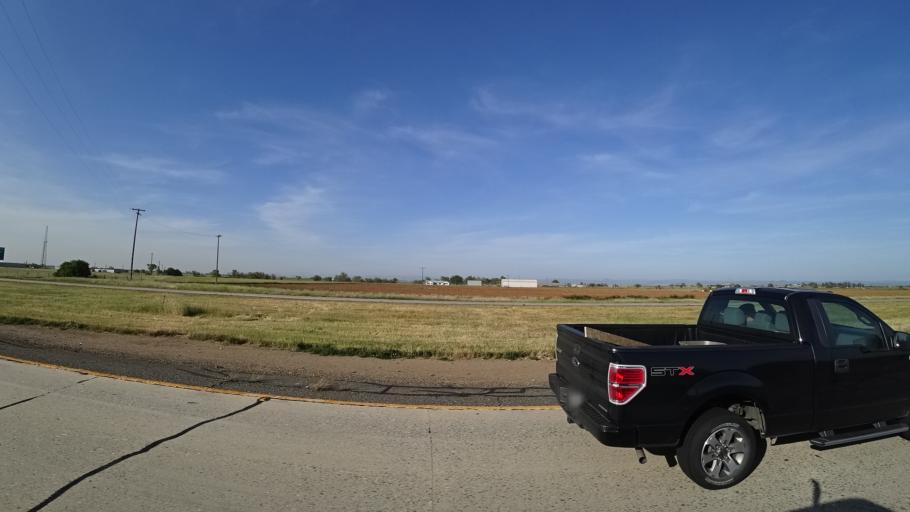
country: US
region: California
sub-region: Yuba County
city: Plumas Lake
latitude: 39.0527
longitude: -121.4966
